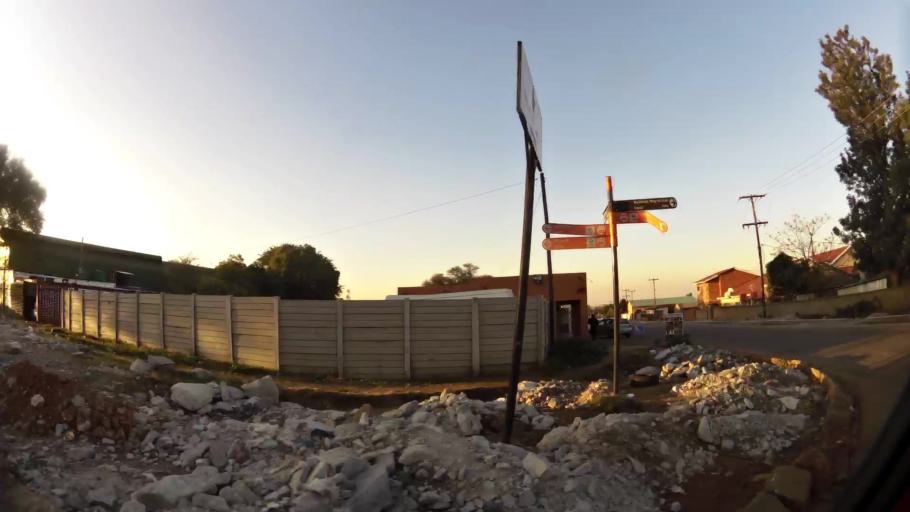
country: ZA
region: North-West
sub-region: Bojanala Platinum District Municipality
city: Rustenburg
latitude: -25.6449
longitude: 27.2135
